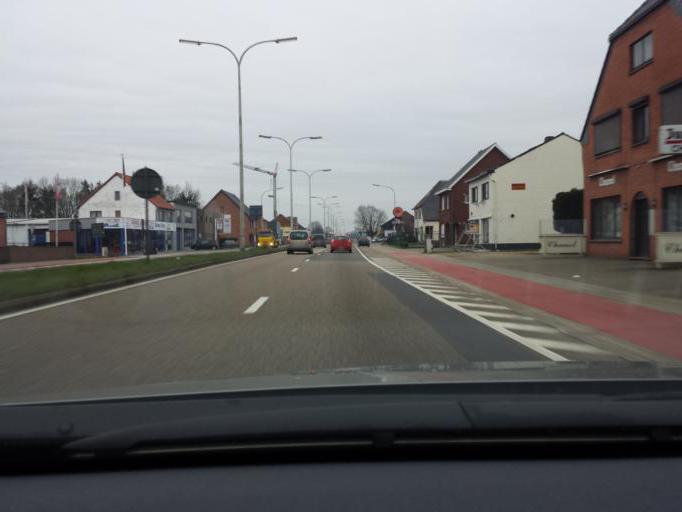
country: BE
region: Flanders
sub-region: Provincie Limburg
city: Houthalen
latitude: 51.0390
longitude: 5.3787
